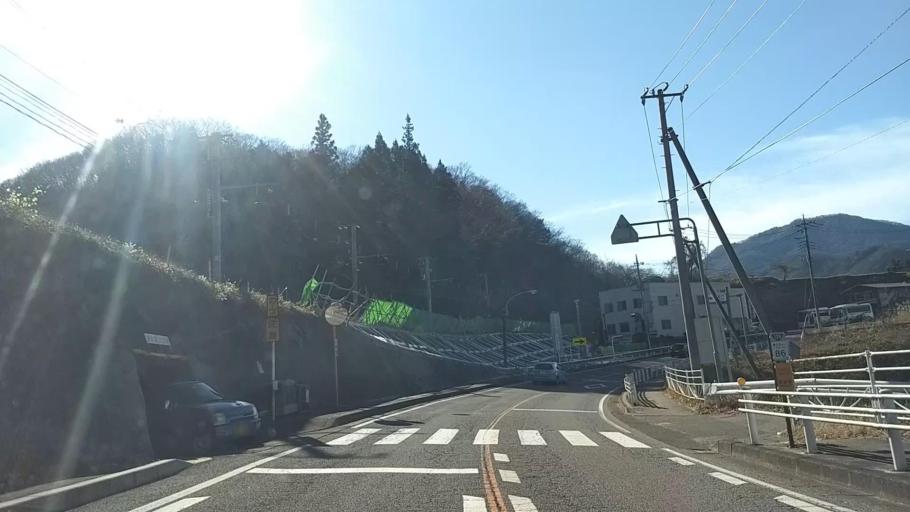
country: JP
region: Yamanashi
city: Otsuki
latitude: 35.6034
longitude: 138.9412
